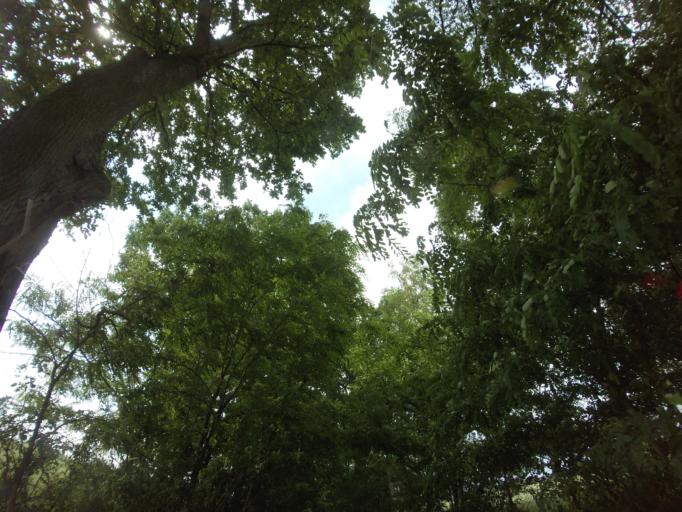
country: PL
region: West Pomeranian Voivodeship
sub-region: Powiat choszczenski
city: Krzecin
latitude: 53.1307
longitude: 15.5867
